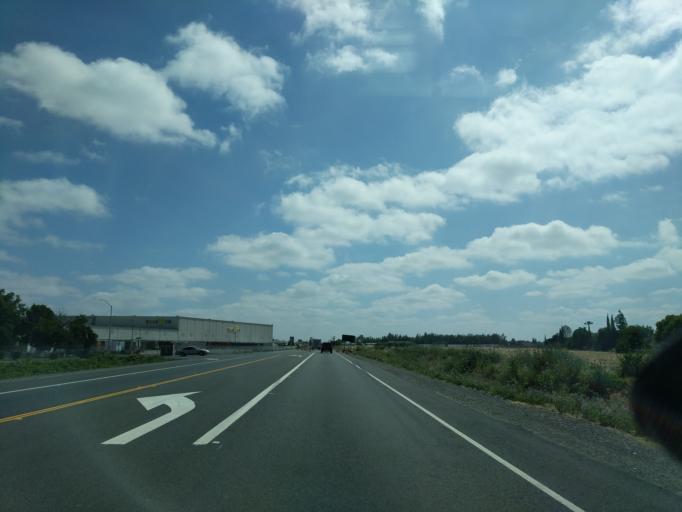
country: US
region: California
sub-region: San Joaquin County
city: Country Club
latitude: 37.9297
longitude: -121.3242
